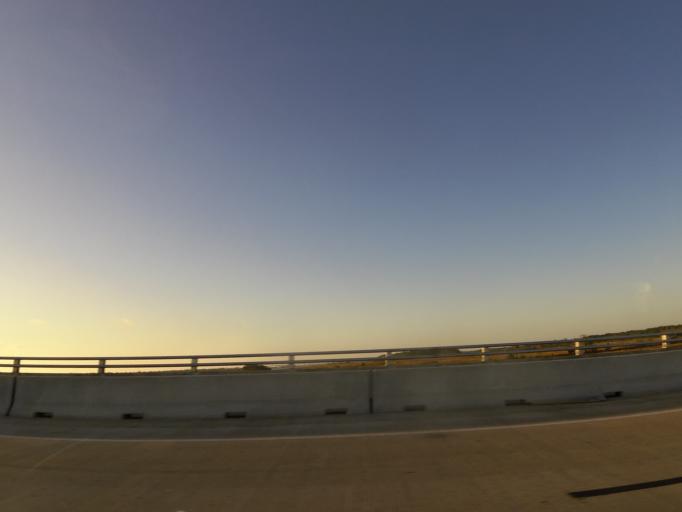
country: US
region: Florida
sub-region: Duval County
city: Atlantic Beach
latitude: 30.3246
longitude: -81.4344
